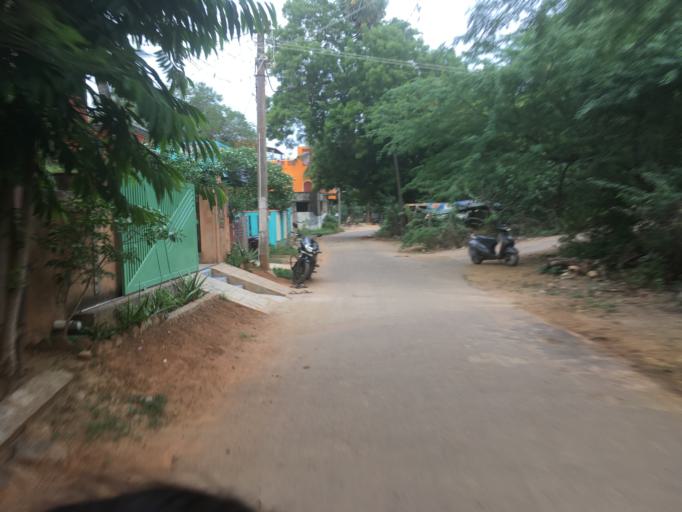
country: IN
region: Tamil Nadu
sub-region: Villupuram
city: Auroville
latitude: 12.0115
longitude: 79.8005
